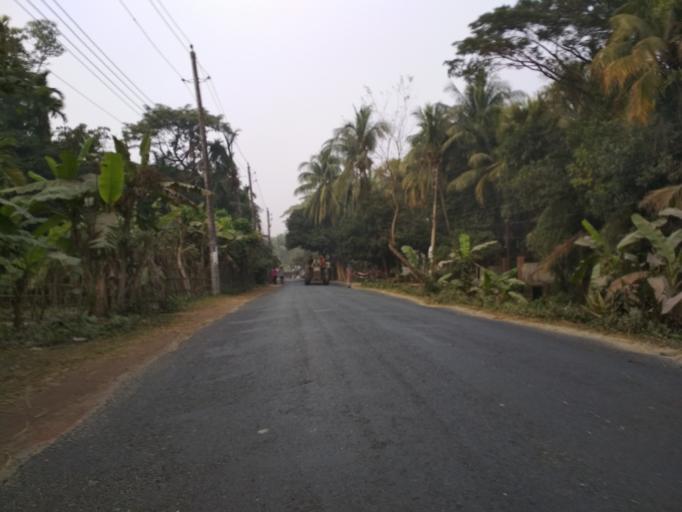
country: BD
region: Chittagong
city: Lakshmipur
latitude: 22.9271
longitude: 90.8338
